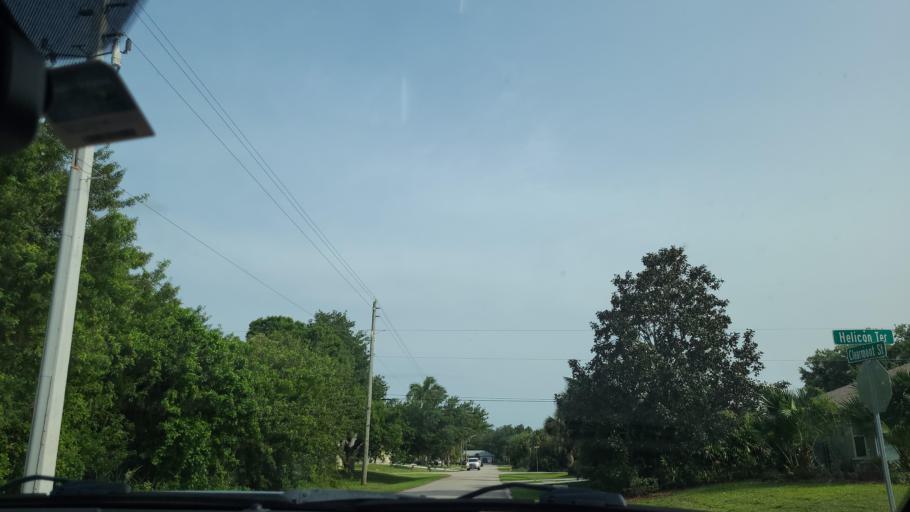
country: US
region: Florida
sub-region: Indian River County
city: Sebastian
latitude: 27.7717
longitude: -80.4915
